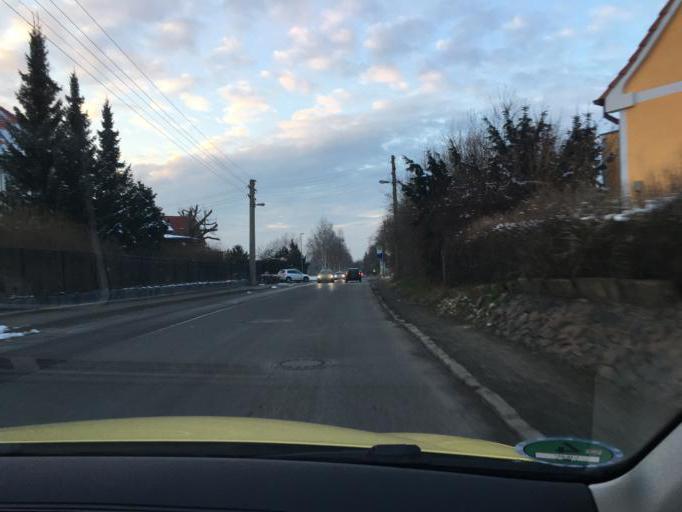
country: DE
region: Saxony
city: Grossposna
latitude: 51.3098
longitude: 12.4533
